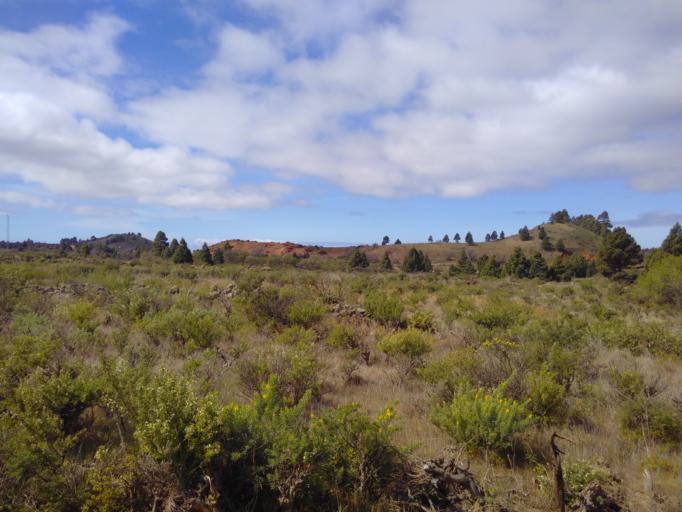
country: ES
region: Canary Islands
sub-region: Provincia de Santa Cruz de Tenerife
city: El Paso
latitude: 28.6609
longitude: -17.8447
